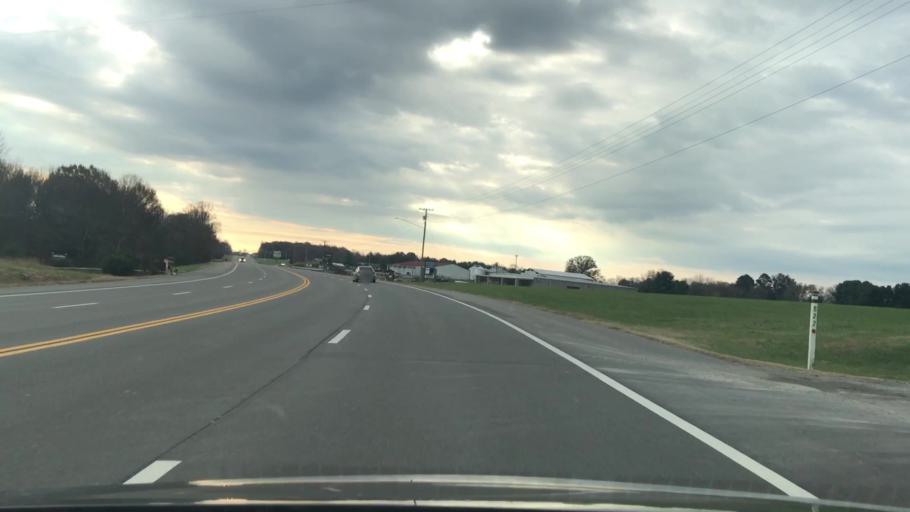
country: US
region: Tennessee
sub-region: Macon County
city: Lafayette
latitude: 36.5094
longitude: -86.0104
